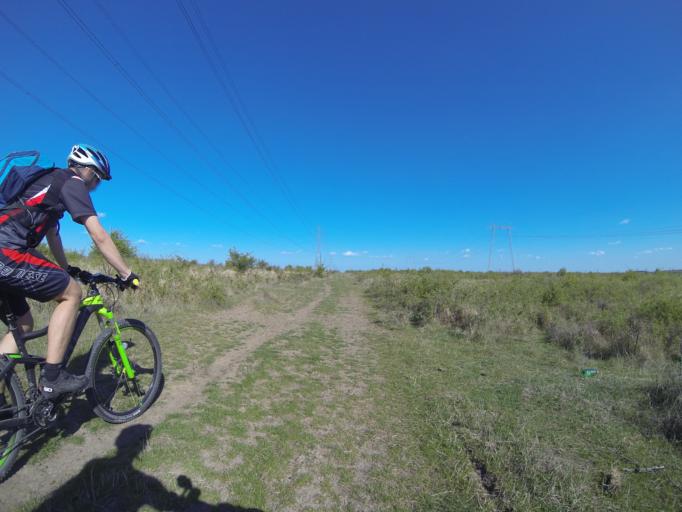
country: RO
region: Dolj
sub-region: Comuna Goesti
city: Goesti
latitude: 44.5163
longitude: 23.7748
